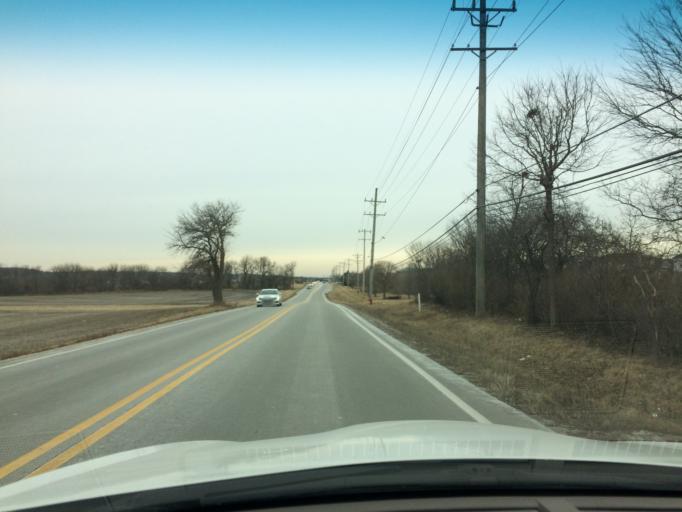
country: US
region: Illinois
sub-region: Kane County
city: Geneva
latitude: 41.8915
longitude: -88.3597
